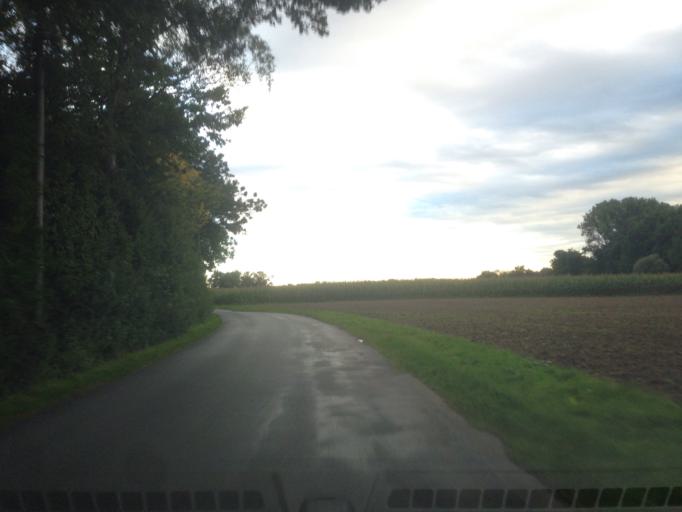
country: DE
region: North Rhine-Westphalia
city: Olfen
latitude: 51.7259
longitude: 7.3743
